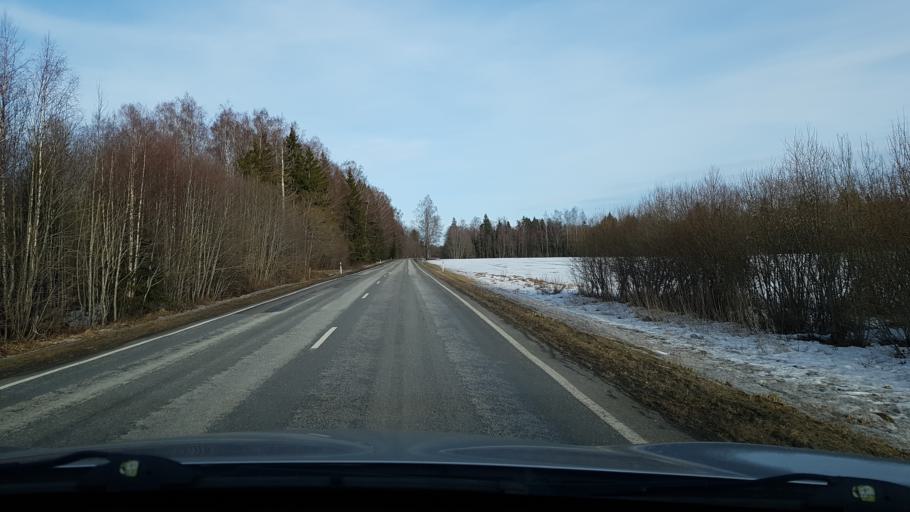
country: EE
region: Viljandimaa
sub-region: Abja vald
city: Abja-Paluoja
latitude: 58.3423
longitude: 25.3526
